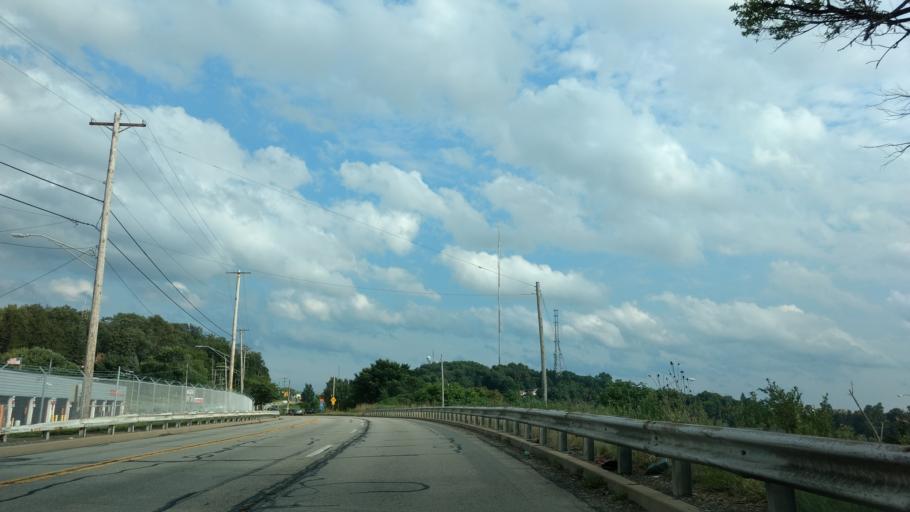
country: US
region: Pennsylvania
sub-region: Allegheny County
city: West View
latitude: 40.5014
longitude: -80.0234
